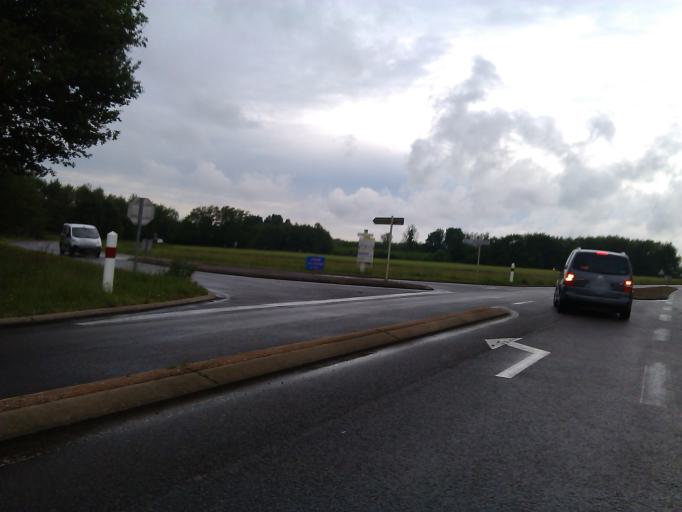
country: FR
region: Bourgogne
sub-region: Departement de Saone-et-Loire
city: Sassenay
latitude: 46.8441
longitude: 4.9406
